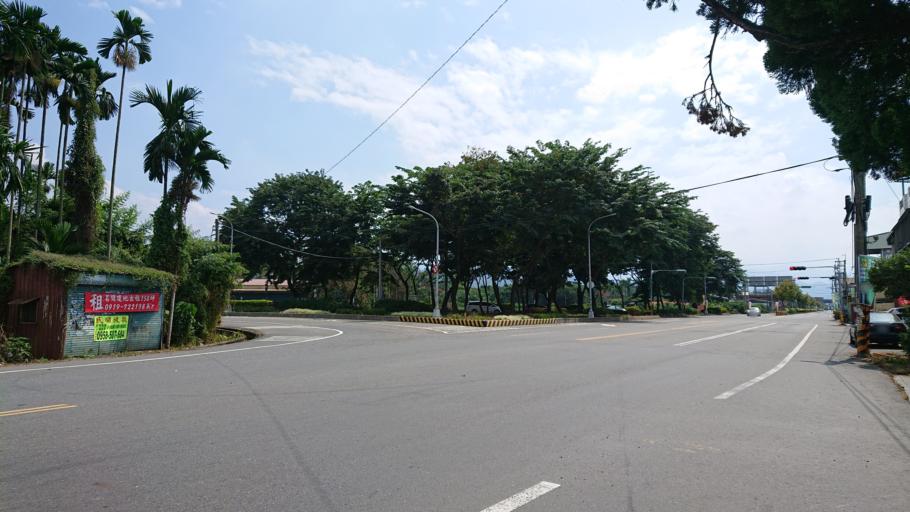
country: TW
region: Taiwan
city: Lugu
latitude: 23.8272
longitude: 120.7049
